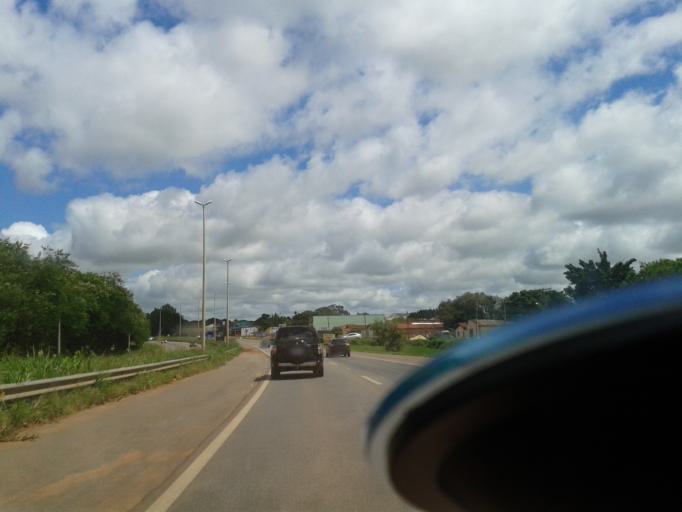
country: BR
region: Goias
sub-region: Goianira
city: Goianira
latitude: -16.5435
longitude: -49.4033
